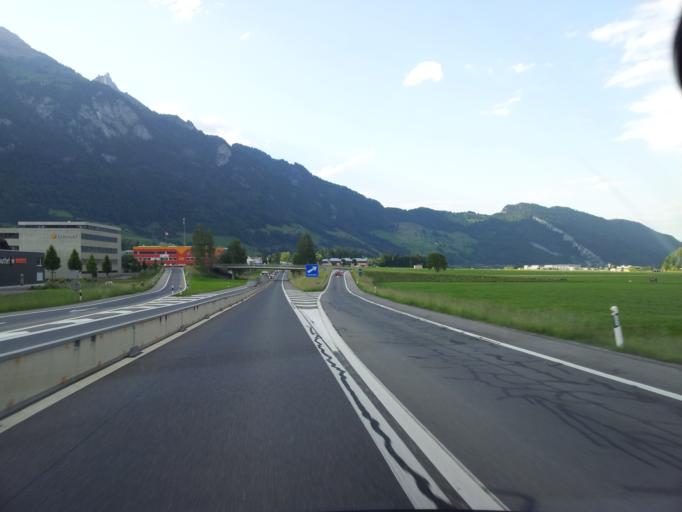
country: CH
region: Obwalden
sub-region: Obwalden
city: Alpnach
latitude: 46.9330
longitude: 8.2772
